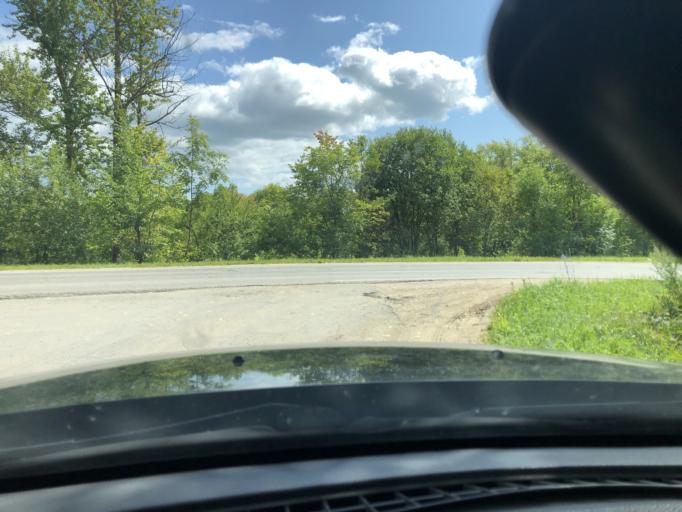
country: RU
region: Tula
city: Revyakino
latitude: 54.3470
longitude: 37.6179
